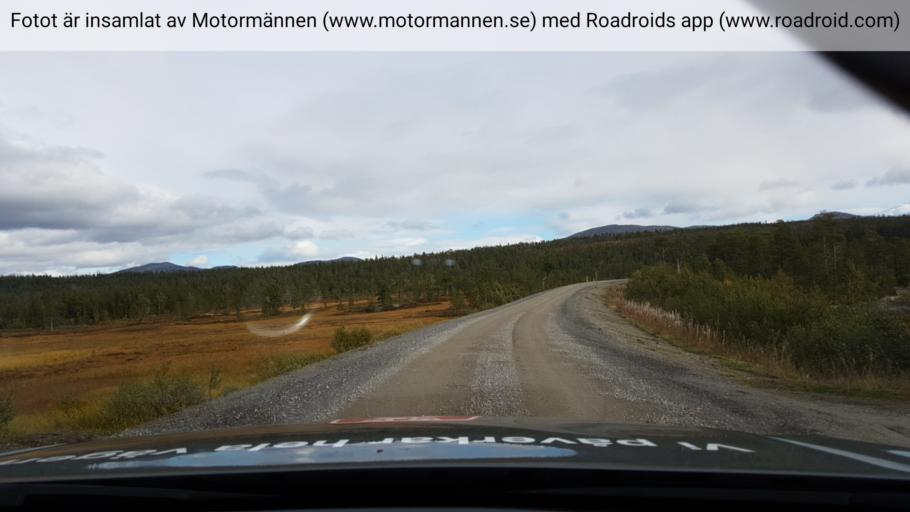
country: NO
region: Nord-Trondelag
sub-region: Snasa
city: Snaase
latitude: 63.7354
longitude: 12.4702
